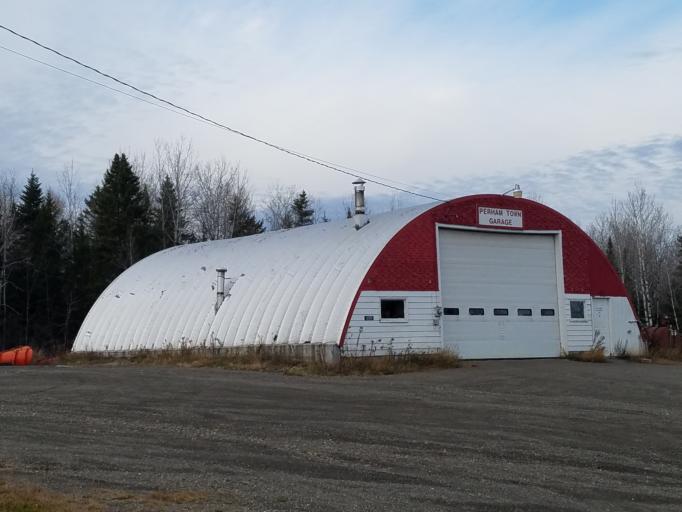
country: US
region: Maine
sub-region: Aroostook County
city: Caribou
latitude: 46.8425
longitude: -68.1946
